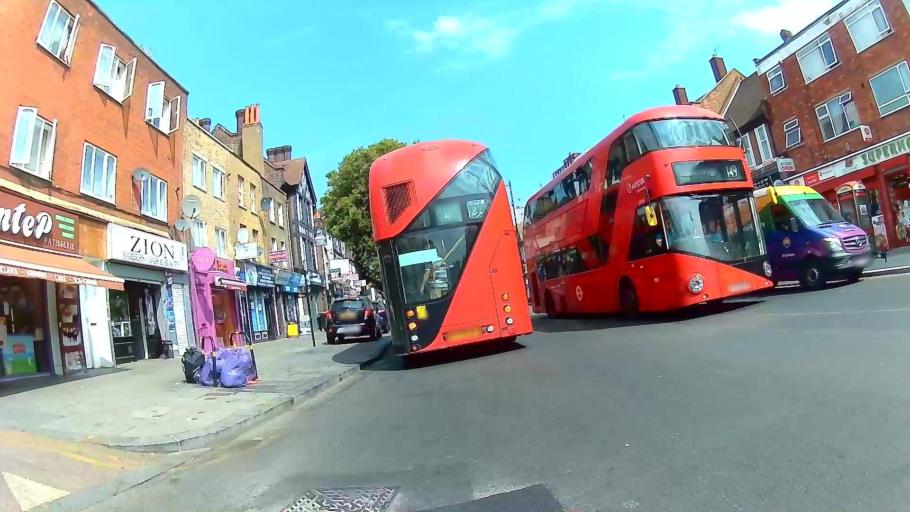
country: GB
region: England
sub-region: Greater London
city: Harringay
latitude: 51.6066
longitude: -0.0682
